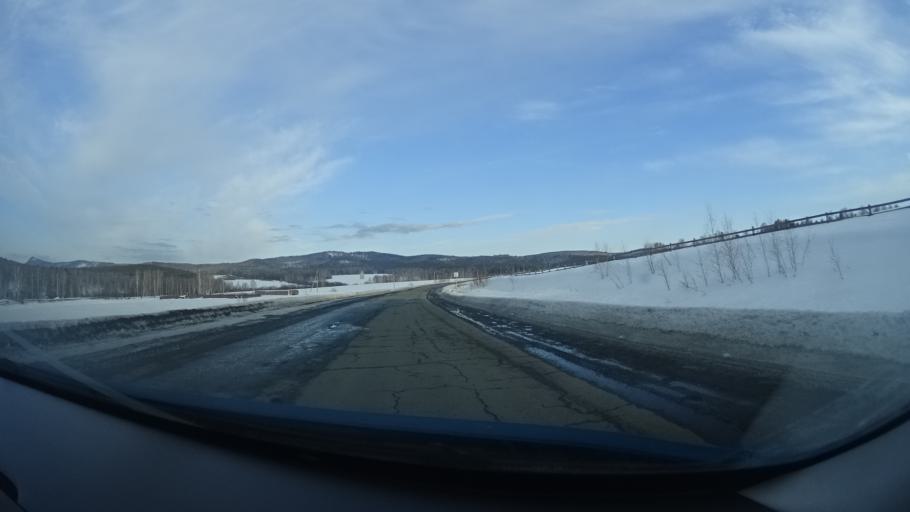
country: RU
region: Bashkortostan
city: Lomovka
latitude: 53.7218
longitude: 58.2487
